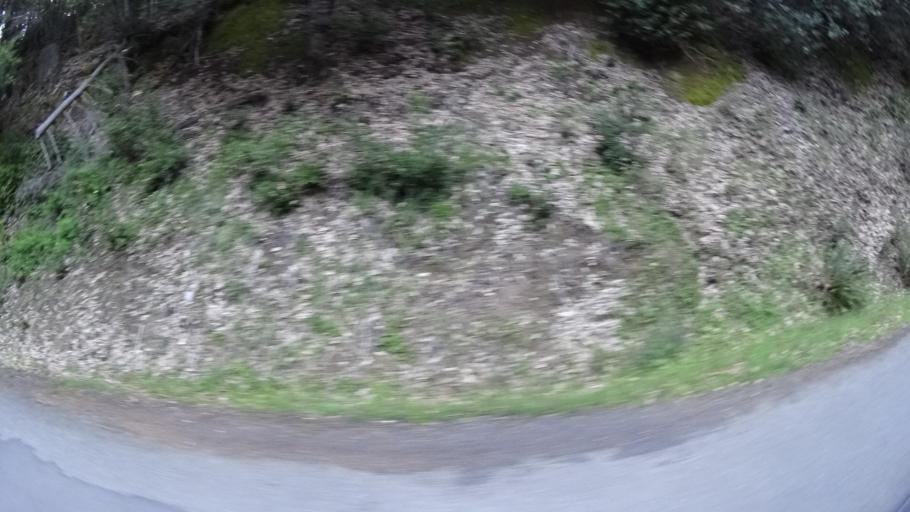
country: US
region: California
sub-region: Humboldt County
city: Blue Lake
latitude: 40.7008
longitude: -123.9406
